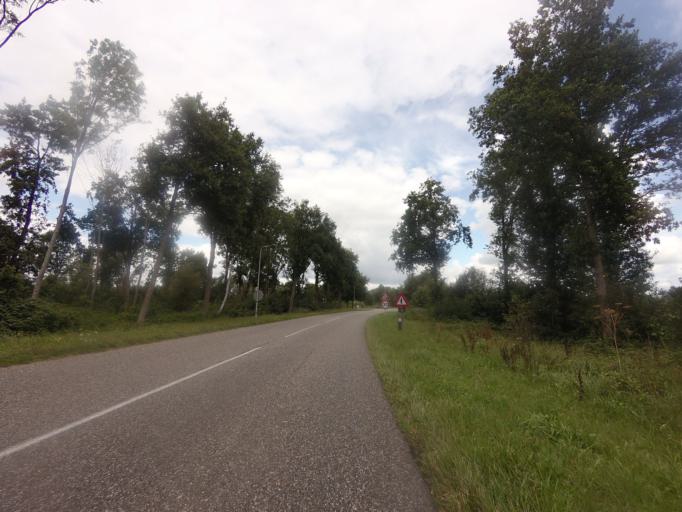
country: NL
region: Drenthe
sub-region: Gemeente Meppel
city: Meppel
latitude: 52.6827
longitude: 6.2140
